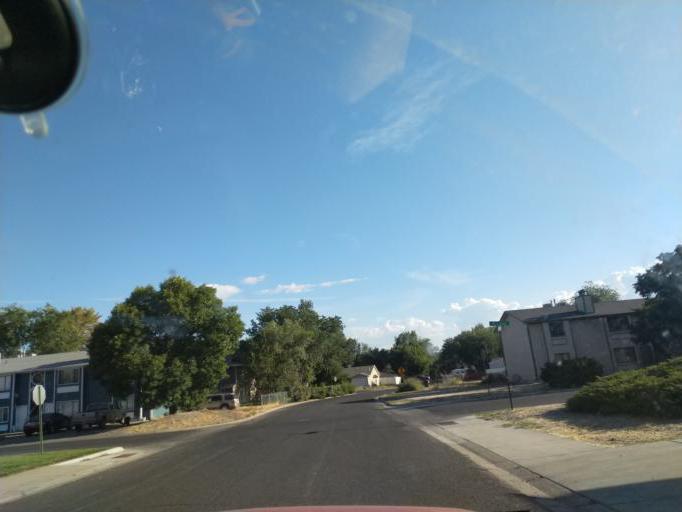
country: US
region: Colorado
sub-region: Mesa County
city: Clifton
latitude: 39.0741
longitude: -108.4566
